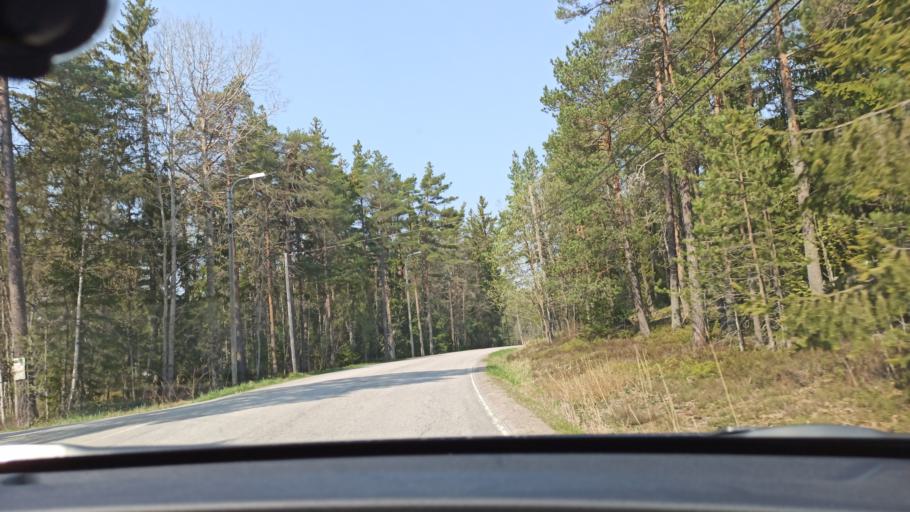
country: FI
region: Uusimaa
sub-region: Helsinki
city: Kirkkonummi
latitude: 60.0944
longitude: 24.5694
